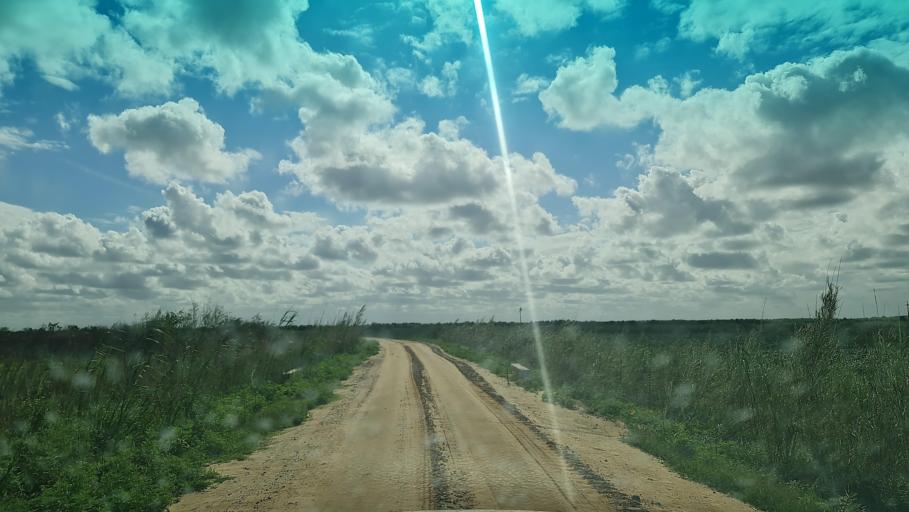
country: MZ
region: Maputo
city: Manhica
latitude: -25.4335
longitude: 32.8638
